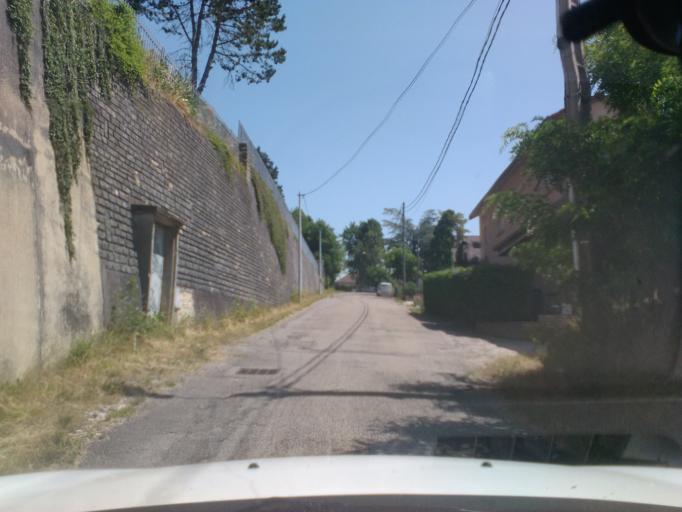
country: FR
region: Lorraine
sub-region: Departement des Vosges
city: Neufchateau
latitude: 48.3580
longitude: 5.7074
